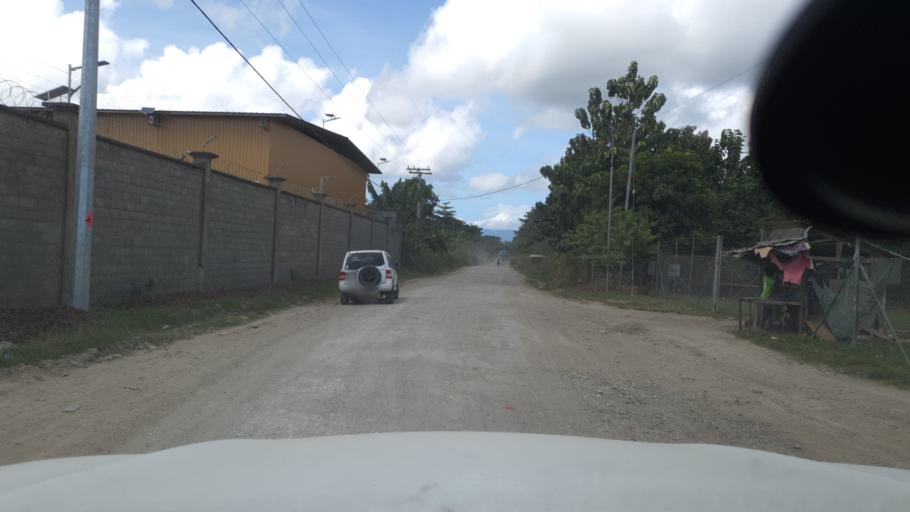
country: SB
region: Guadalcanal
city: Honiara
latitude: -9.4249
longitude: 160.0378
